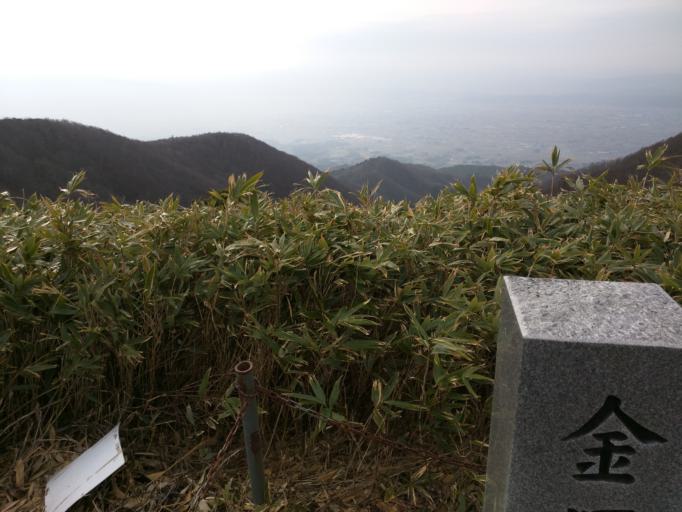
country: JP
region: Fukushima
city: Kitakata
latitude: 37.6206
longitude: 139.9954
